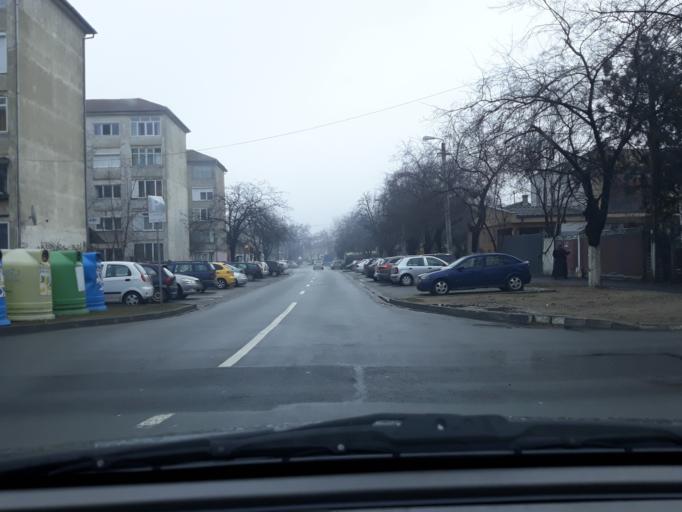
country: RO
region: Bihor
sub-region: Comuna Biharea
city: Oradea
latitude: 47.0436
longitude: 21.9561
